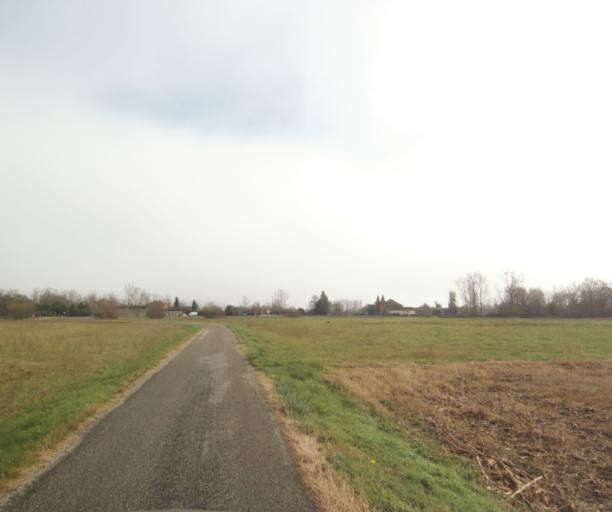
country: FR
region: Midi-Pyrenees
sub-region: Departement de la Haute-Garonne
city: Villemur-sur-Tarn
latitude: 43.8521
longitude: 1.4940
